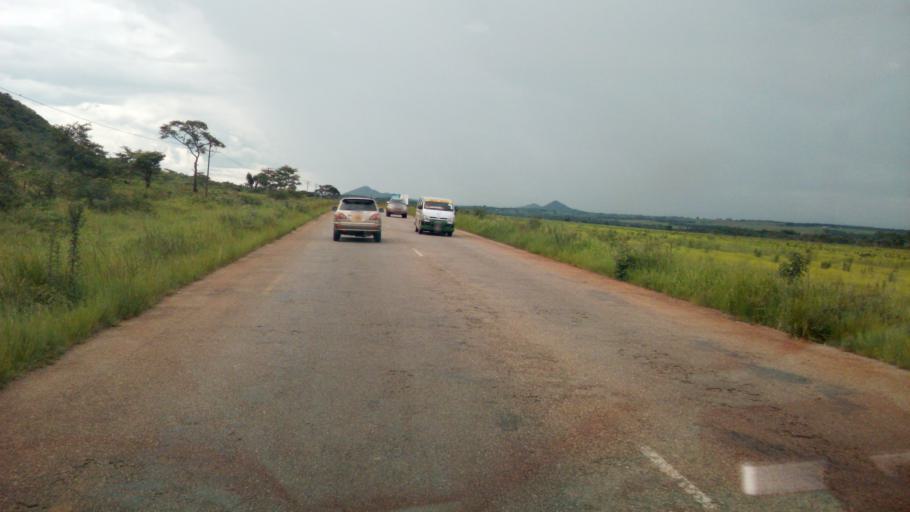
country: ZW
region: Mashonaland Central
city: Bindura
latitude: -17.3050
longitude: 31.2854
